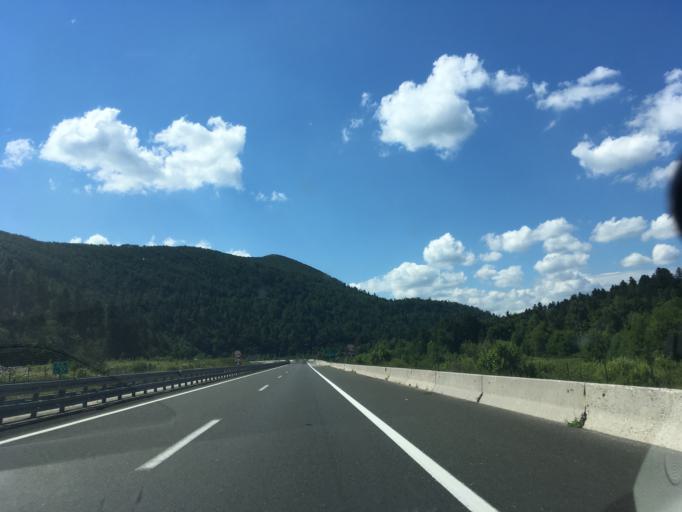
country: HR
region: Primorsko-Goranska
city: Hreljin
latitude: 45.3222
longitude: 14.6631
